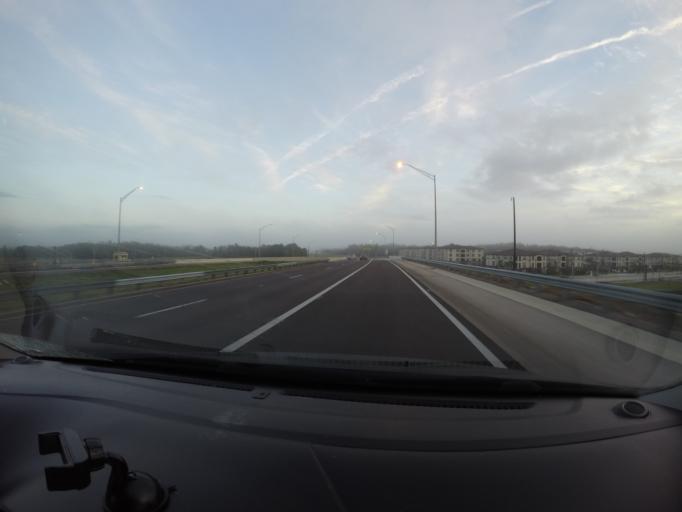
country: US
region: Florida
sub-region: Orange County
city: Conway
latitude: 28.4136
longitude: -81.2279
